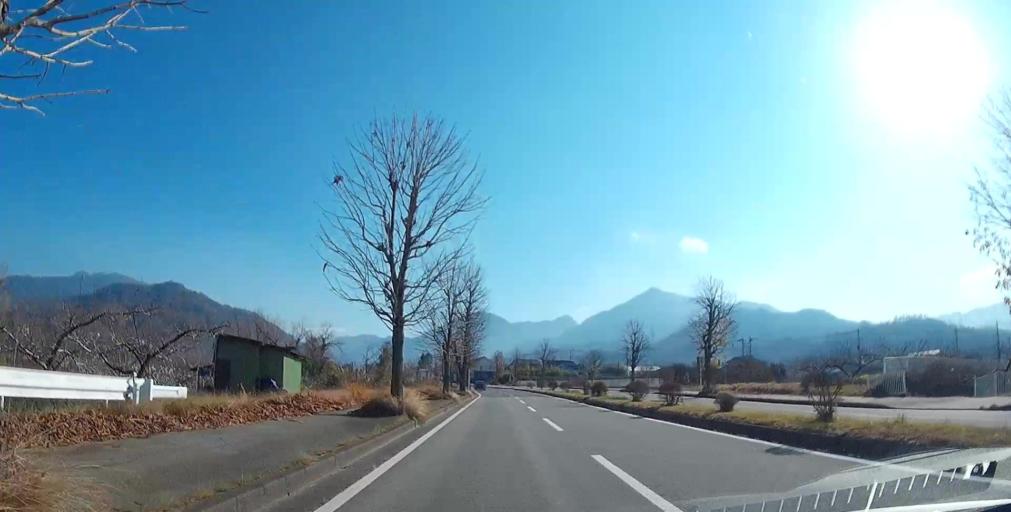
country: JP
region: Yamanashi
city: Isawa
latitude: 35.6248
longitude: 138.6860
